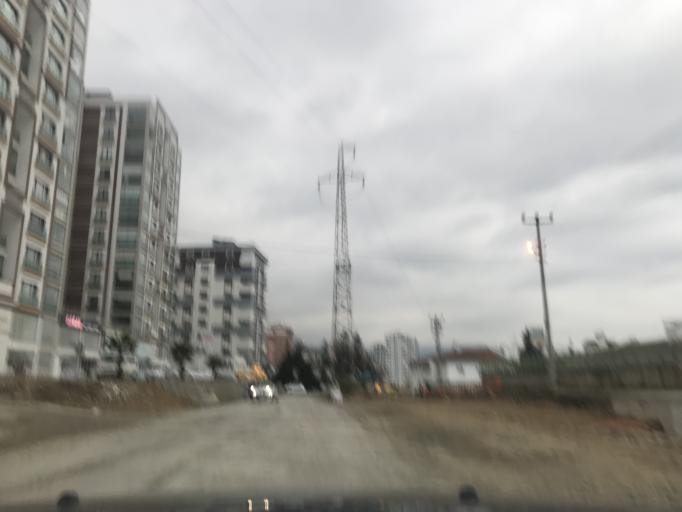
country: TR
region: Trabzon
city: Akcaabat
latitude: 41.0070
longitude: 39.6105
